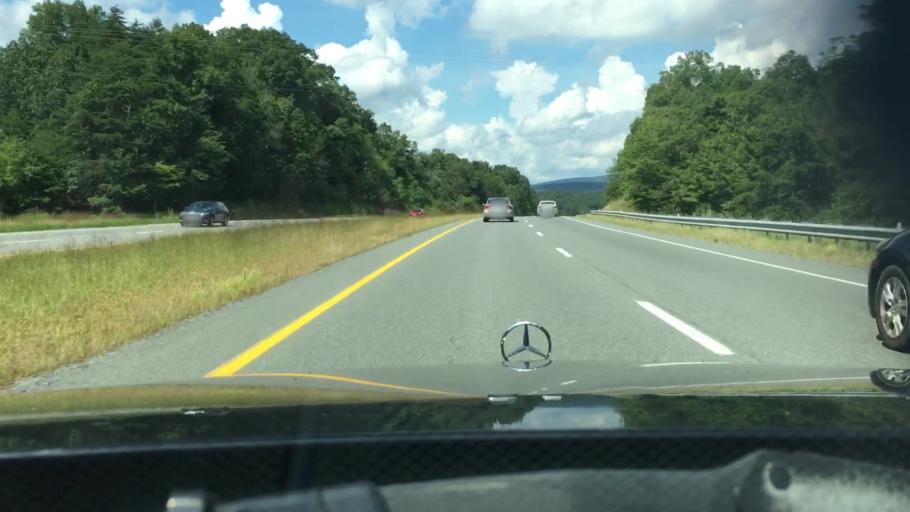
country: US
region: Virginia
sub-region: Frederick County
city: Shawnee Land
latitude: 39.3256
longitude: -78.3019
